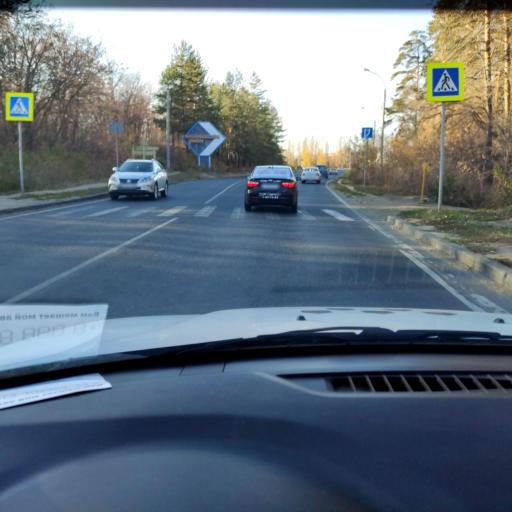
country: RU
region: Samara
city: Tol'yatti
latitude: 53.4941
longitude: 49.2922
